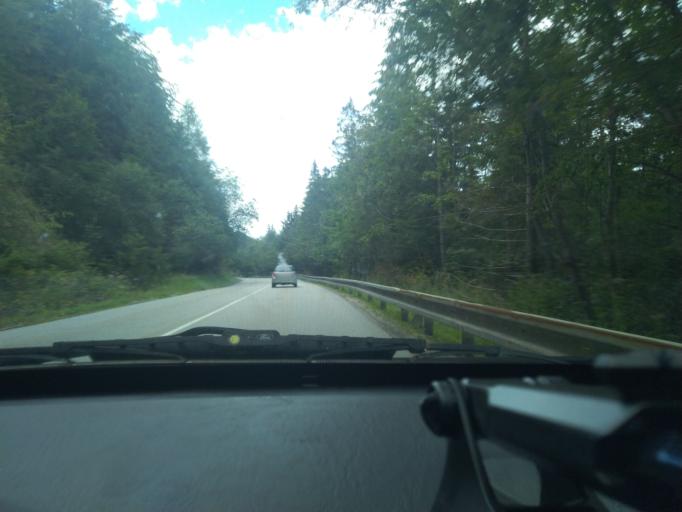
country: SK
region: Banskobystricky
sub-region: Okres Ziar nad Hronom
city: Kremnica
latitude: 48.8361
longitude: 18.9680
